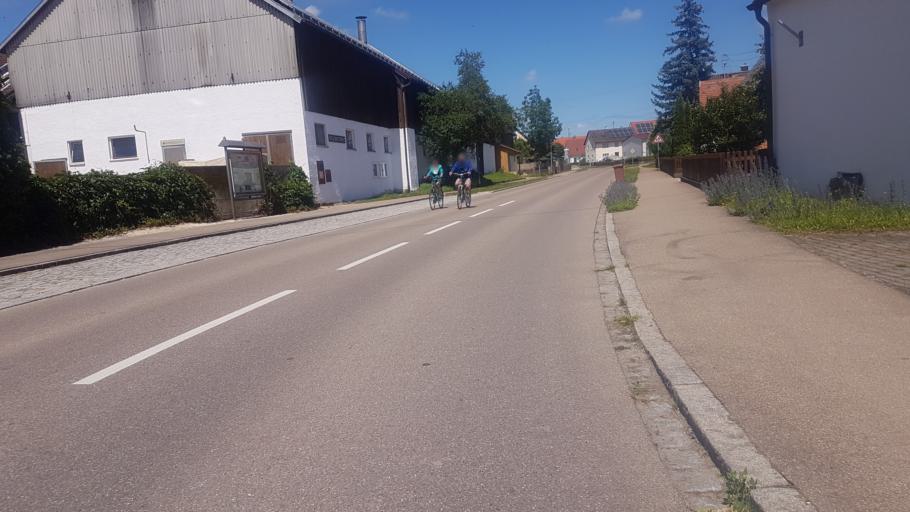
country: DE
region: Bavaria
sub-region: Swabia
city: Blindheim
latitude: 48.6320
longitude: 10.6184
